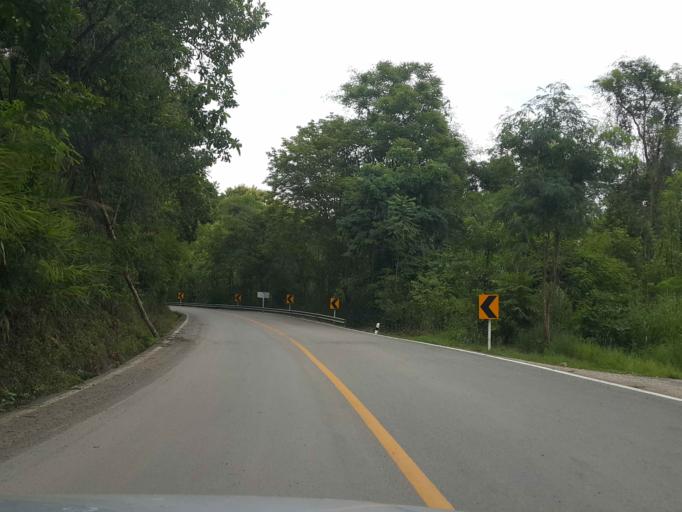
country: TH
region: Lampang
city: Thoen
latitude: 17.6728
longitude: 99.1119
